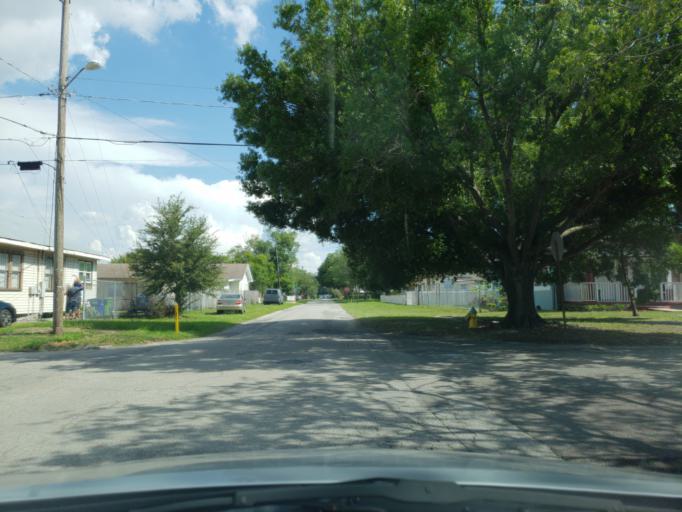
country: US
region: Florida
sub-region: Hillsborough County
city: Tampa
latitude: 27.9712
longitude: -82.4869
